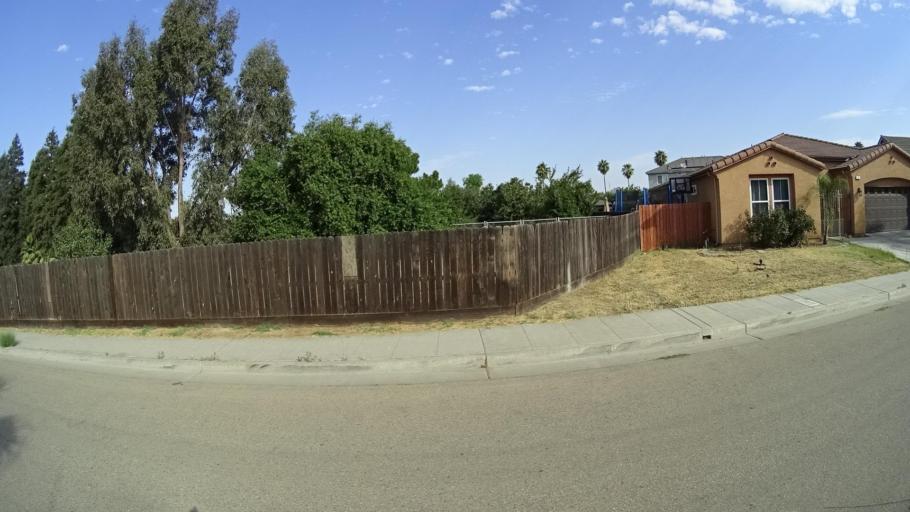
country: US
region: California
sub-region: Fresno County
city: Sunnyside
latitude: 36.7186
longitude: -119.7016
